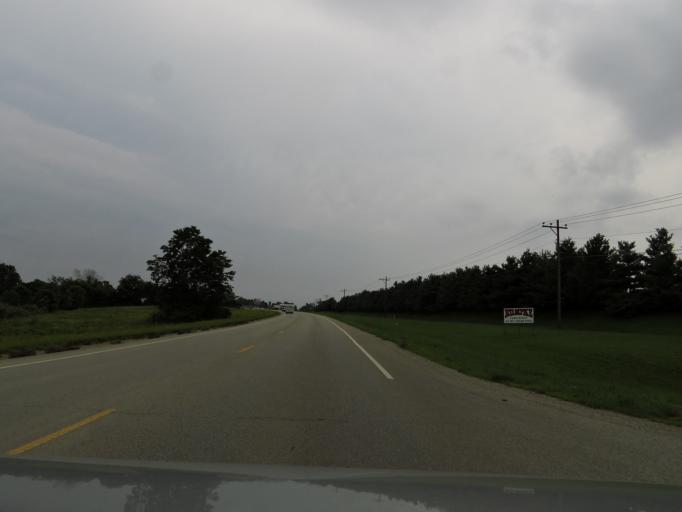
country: US
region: Ohio
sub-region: Brown County
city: Georgetown
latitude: 38.9018
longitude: -83.9023
